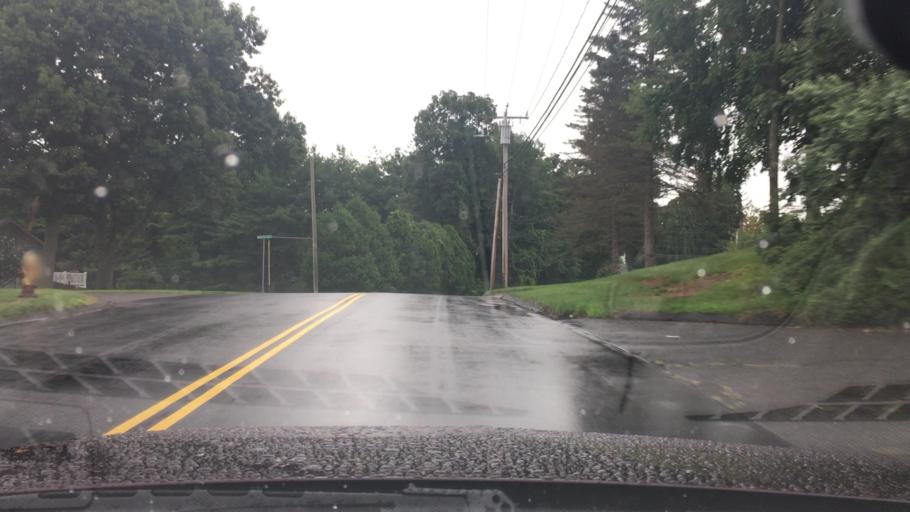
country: US
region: Connecticut
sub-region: New Haven County
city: Cheshire Village
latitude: 41.5284
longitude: -72.9161
